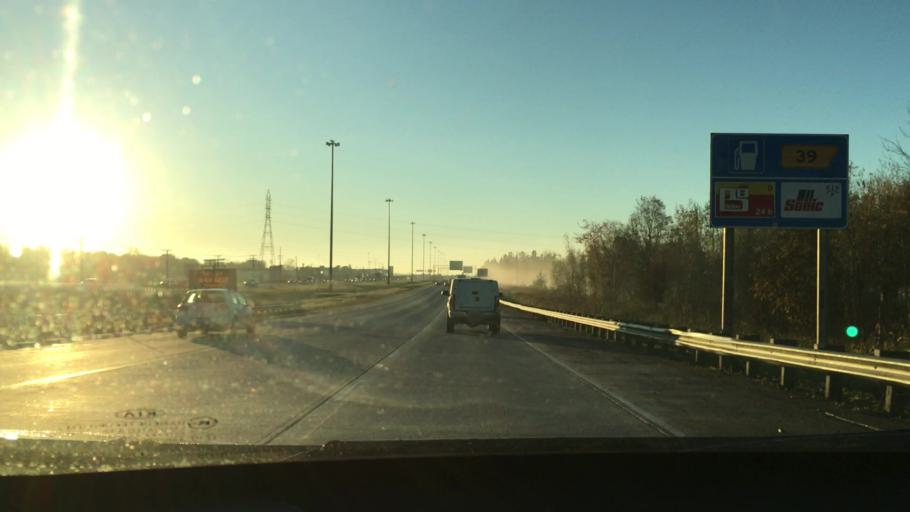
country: CA
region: Quebec
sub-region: Laurentides
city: Saint-Jerome
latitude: 45.7527
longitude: -74.0150
